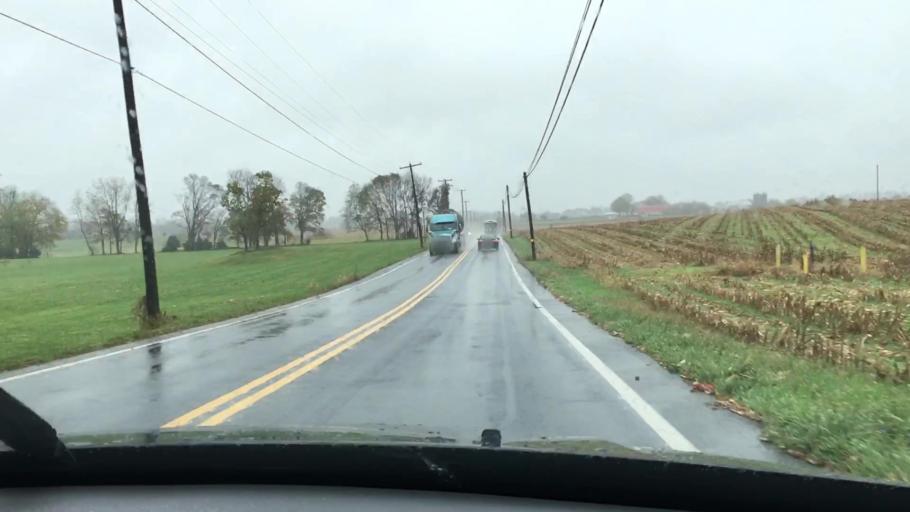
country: US
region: Maryland
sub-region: Frederick County
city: Adamstown
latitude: 39.2754
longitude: -77.4654
